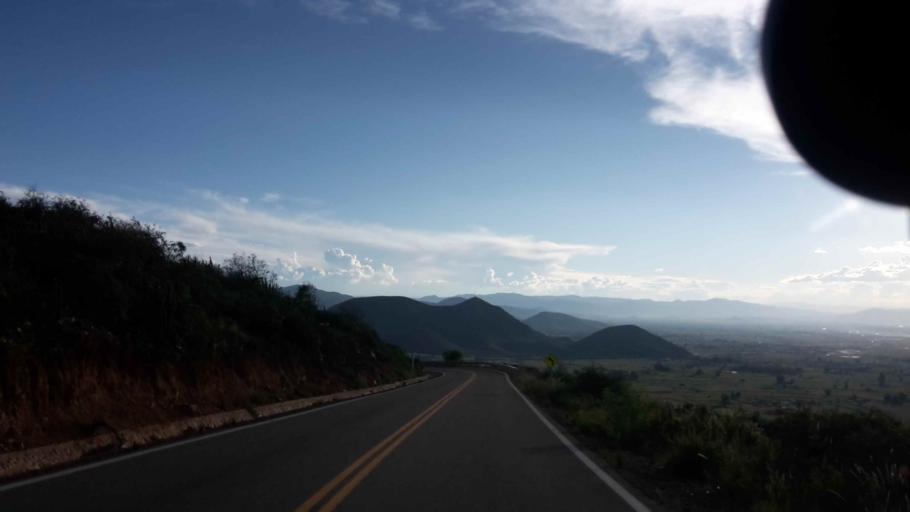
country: BO
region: Cochabamba
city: Arani
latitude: -17.5879
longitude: -65.7525
